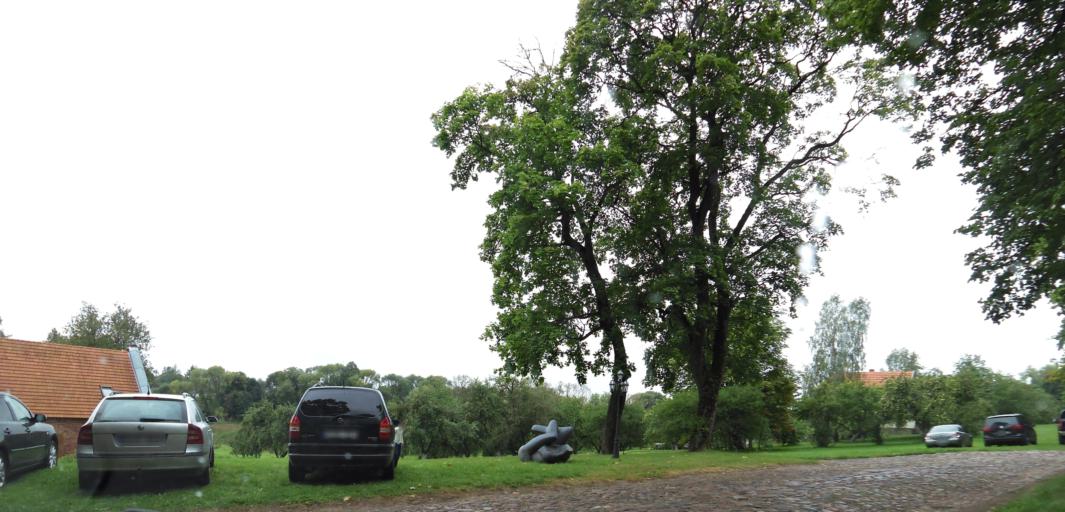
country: LT
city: Sirvintos
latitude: 55.0769
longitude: 25.0622
